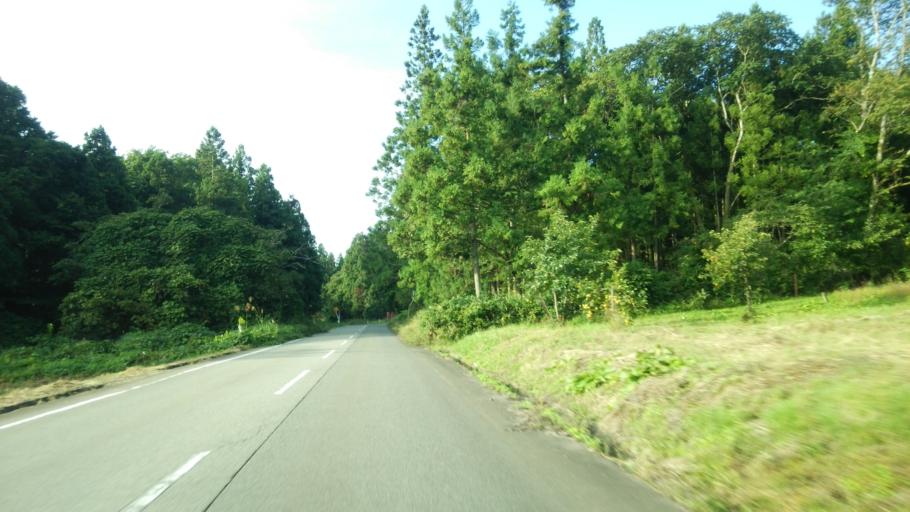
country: JP
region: Fukushima
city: Kitakata
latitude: 37.5882
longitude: 139.8052
